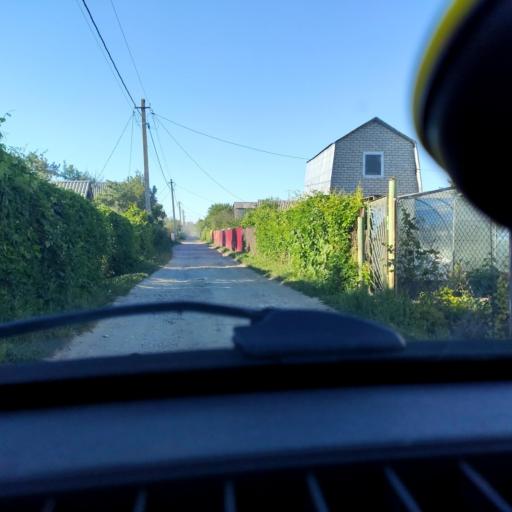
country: RU
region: Samara
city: Tol'yatti
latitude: 53.5914
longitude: 49.3140
